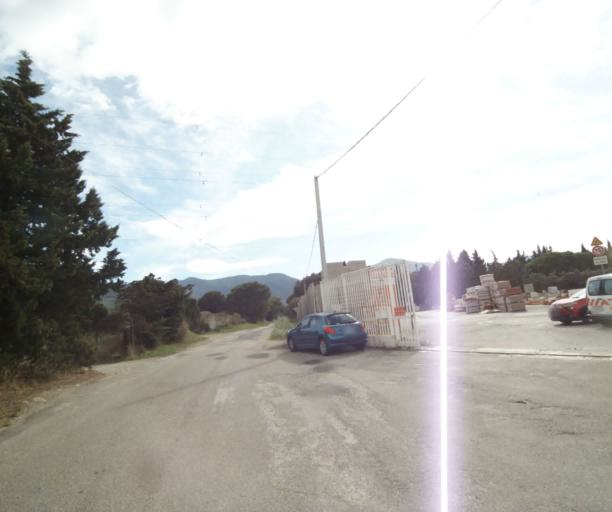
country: FR
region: Languedoc-Roussillon
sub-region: Departement des Pyrenees-Orientales
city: Sant Andreu de Sureda
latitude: 42.5483
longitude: 2.9910
